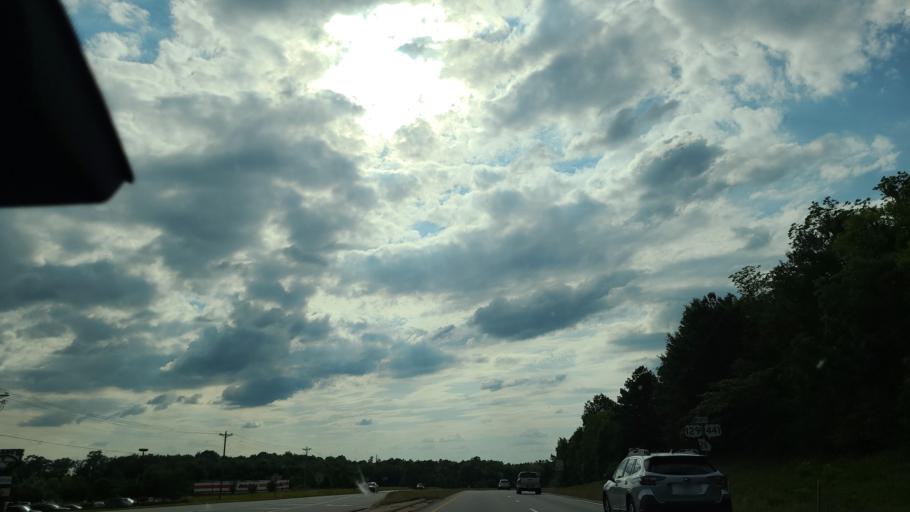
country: US
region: Georgia
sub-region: Putnam County
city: Eatonton
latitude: 33.2973
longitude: -83.3851
